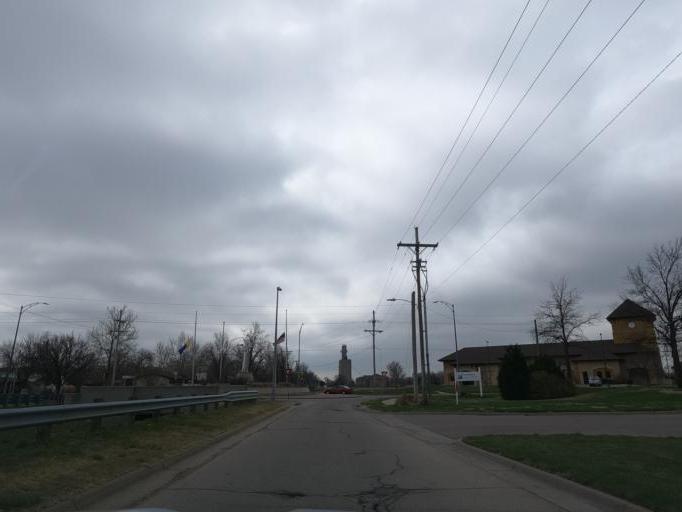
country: US
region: Kansas
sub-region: Reno County
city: Hutchinson
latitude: 38.0798
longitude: -97.9132
